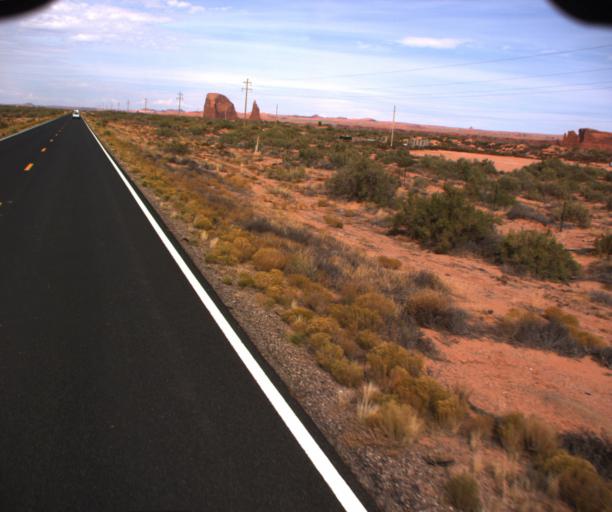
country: US
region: Arizona
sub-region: Apache County
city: Many Farms
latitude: 36.6301
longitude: -109.5848
